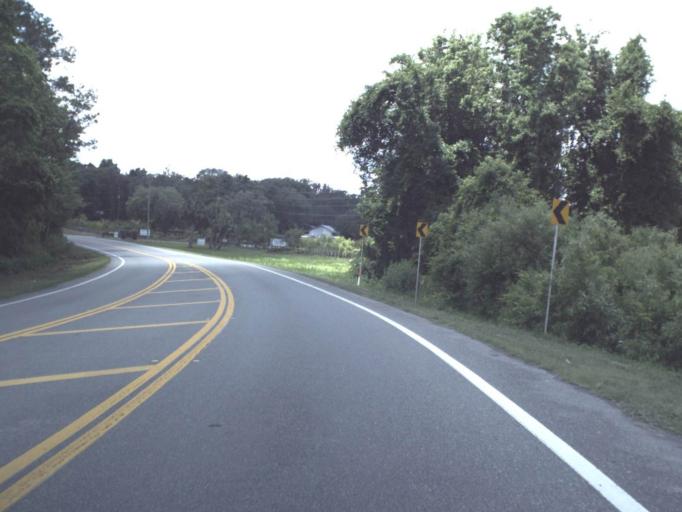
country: US
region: Florida
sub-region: Putnam County
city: Palatka
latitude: 29.5635
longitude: -81.6570
